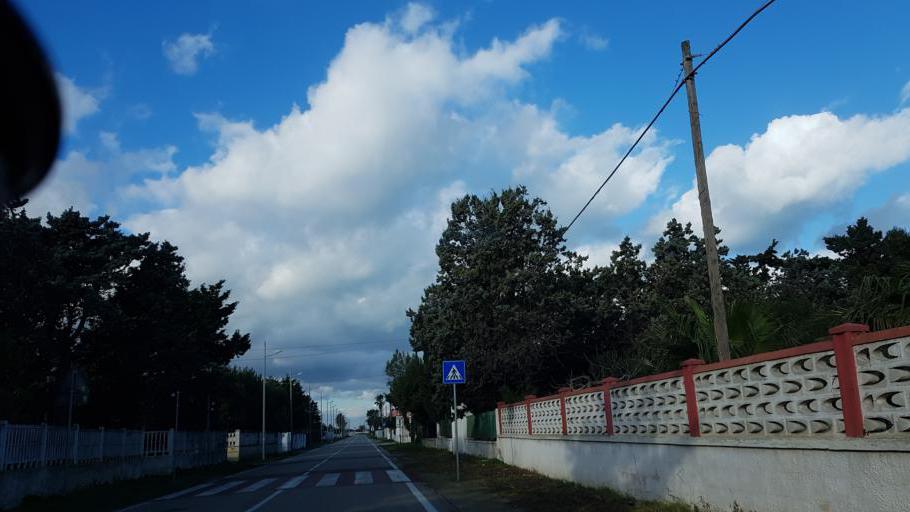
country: IT
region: Apulia
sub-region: Provincia di Brindisi
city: Materdomini
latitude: 40.6786
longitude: 17.9378
